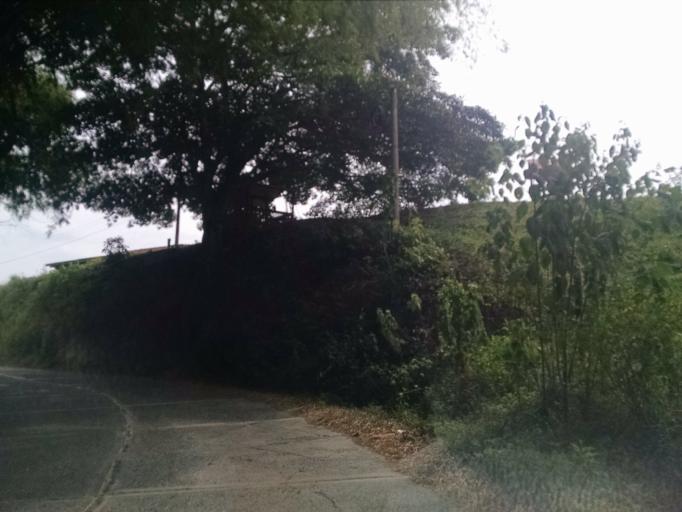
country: CO
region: Valle del Cauca
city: Alcala
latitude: 4.6975
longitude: -75.7740
